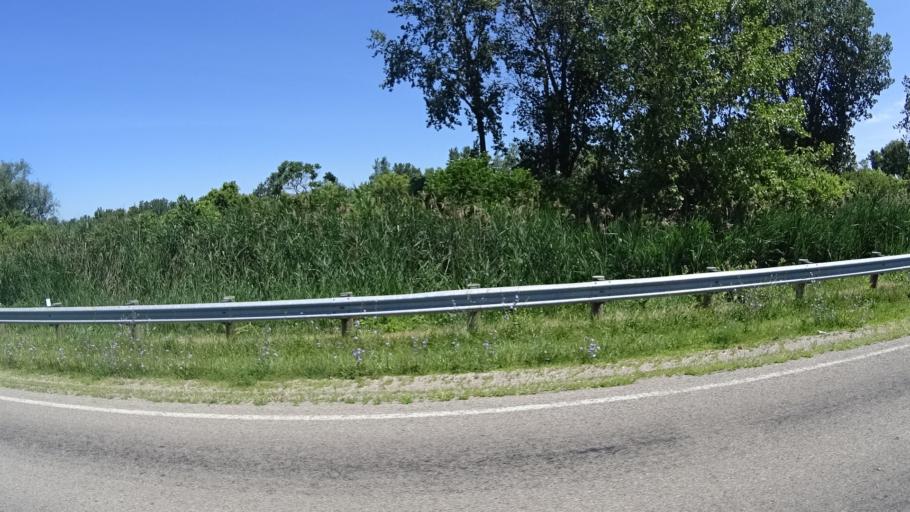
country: US
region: Ohio
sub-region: Erie County
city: Sandusky
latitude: 41.4556
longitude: -82.7860
